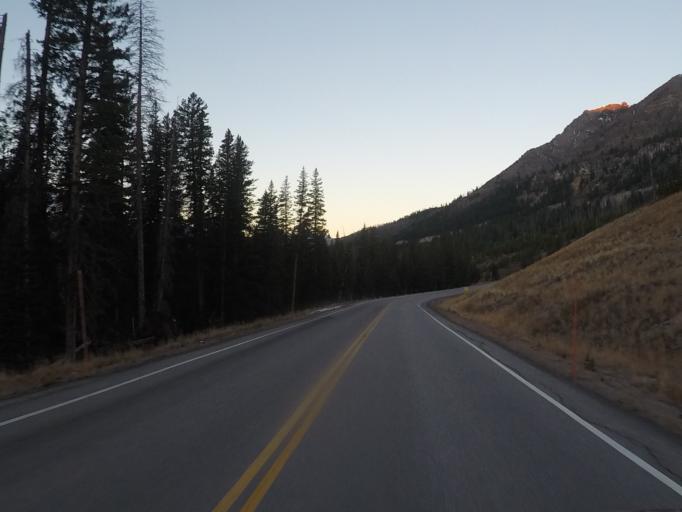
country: US
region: Montana
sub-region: Stillwater County
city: Absarokee
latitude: 45.0184
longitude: -109.9563
